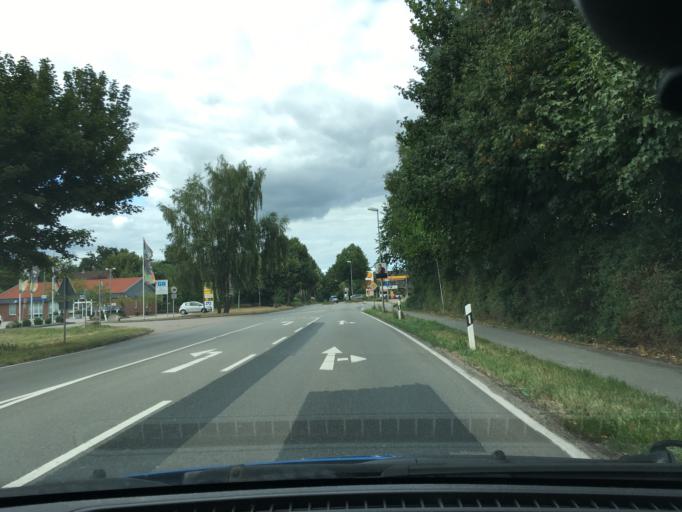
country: DE
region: Lower Saxony
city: Neu Wulmstorf
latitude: 53.4220
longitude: 9.7897
